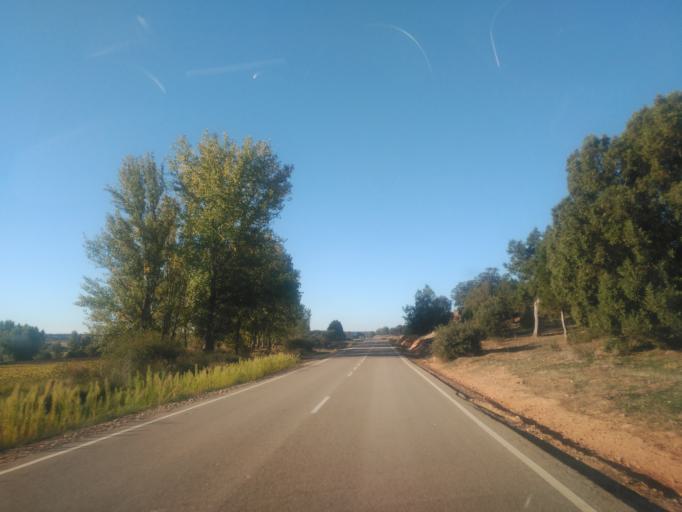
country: ES
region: Castille and Leon
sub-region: Provincia de Soria
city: Alcubilla de Avellaneda
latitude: 41.7334
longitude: -3.2973
